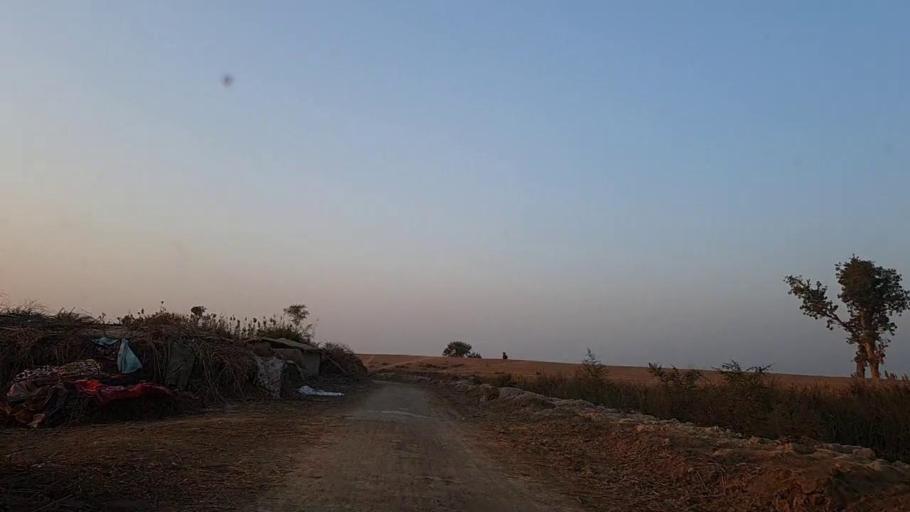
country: PK
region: Sindh
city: Bhit Shah
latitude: 25.9141
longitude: 68.5037
